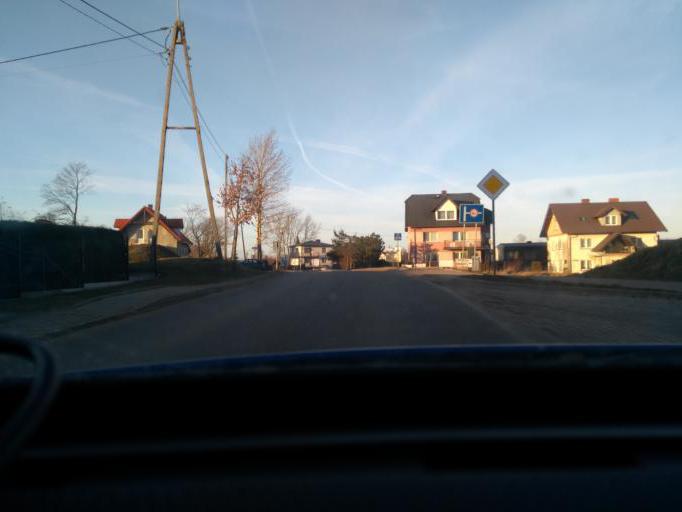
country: PL
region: Pomeranian Voivodeship
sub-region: Powiat kartuski
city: Przodkowo
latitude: 54.3817
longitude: 18.2882
